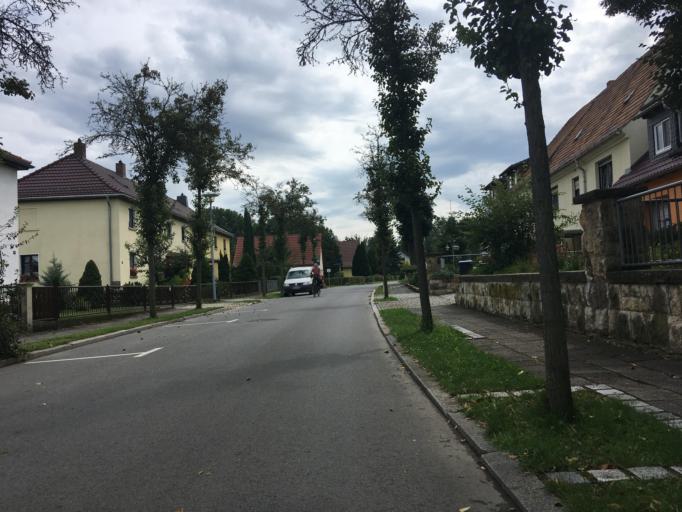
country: DE
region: Saxony
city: Pirna
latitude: 50.9470
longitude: 13.9268
